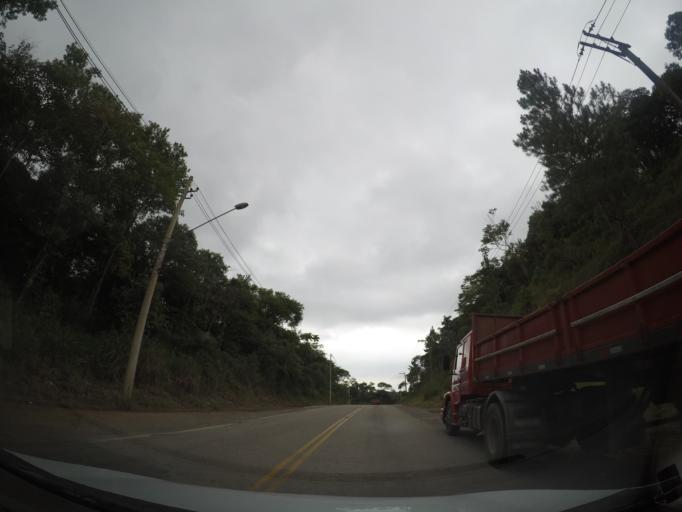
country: BR
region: Sao Paulo
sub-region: Aruja
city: Aruja
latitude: -23.3343
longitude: -46.4016
